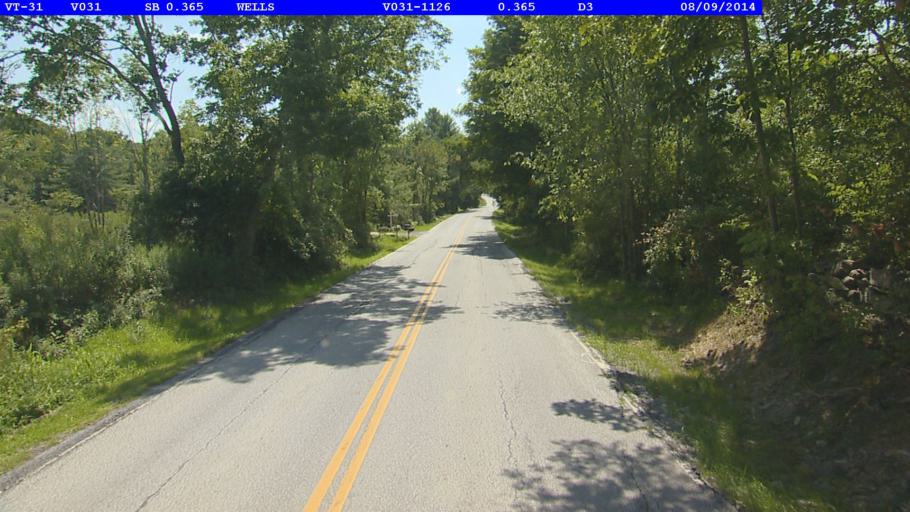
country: US
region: New York
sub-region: Washington County
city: Granville
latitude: 43.4432
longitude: -73.2476
